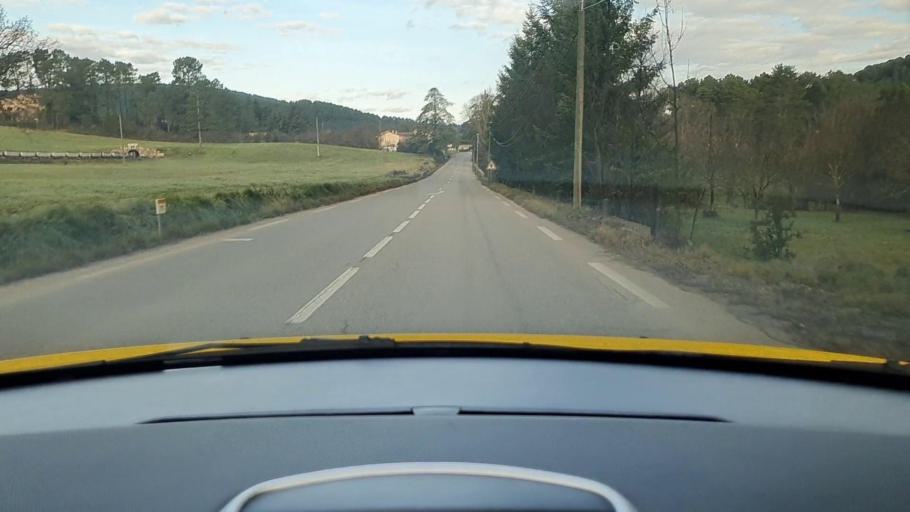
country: FR
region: Languedoc-Roussillon
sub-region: Departement du Gard
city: Laval-Pradel
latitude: 44.2265
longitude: 4.0637
